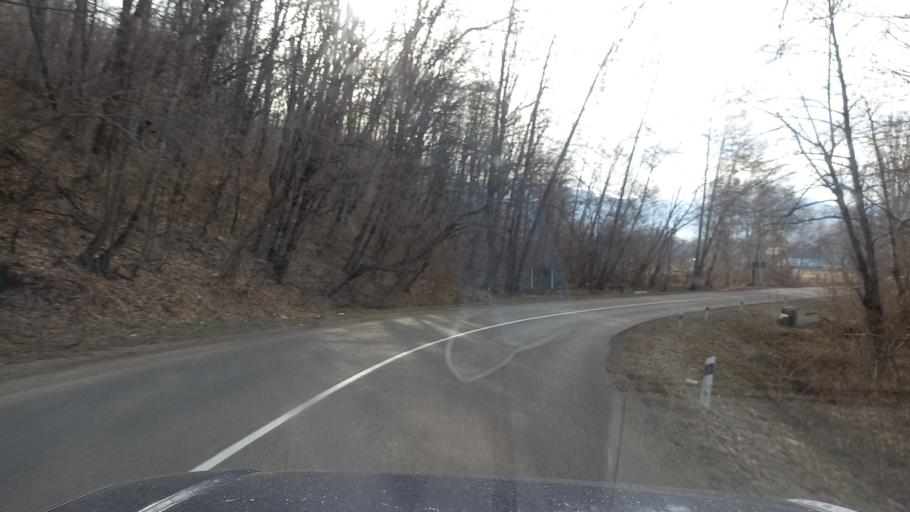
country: RU
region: Krasnodarskiy
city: Neftegorsk
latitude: 44.2841
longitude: 39.9227
